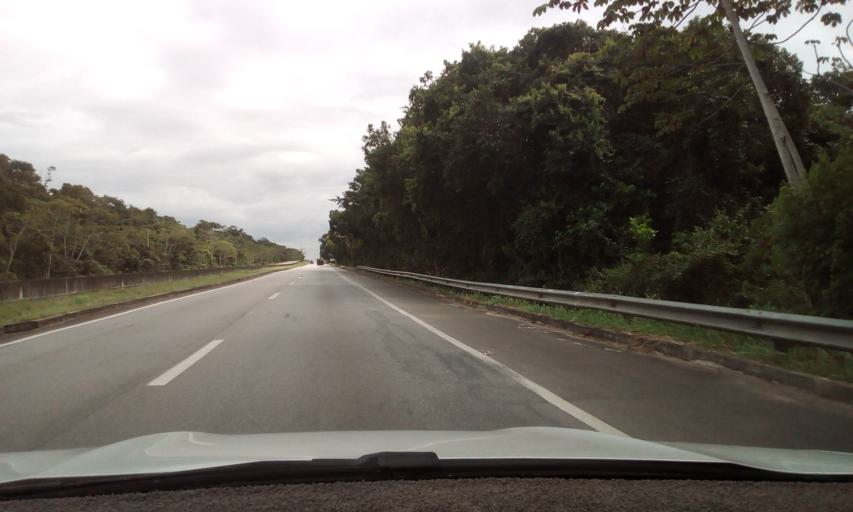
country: BR
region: Paraiba
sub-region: Mamanguape
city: Mamanguape
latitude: -6.9798
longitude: -35.0766
